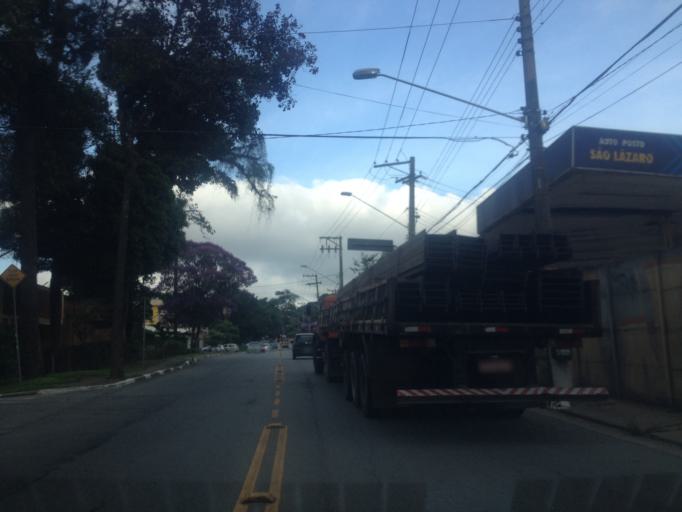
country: BR
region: Sao Paulo
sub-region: Diadema
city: Diadema
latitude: -23.7267
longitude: -46.7152
